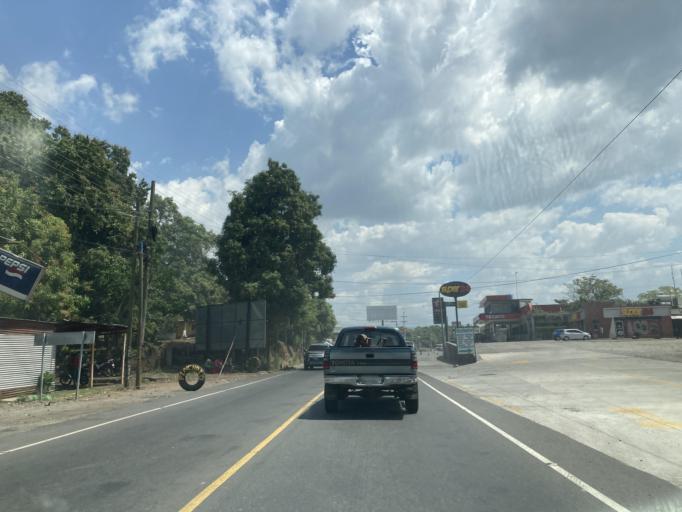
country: GT
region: Santa Rosa
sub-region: Municipio de Chiquimulilla
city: Chiquimulilla
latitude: 14.0685
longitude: -90.3845
